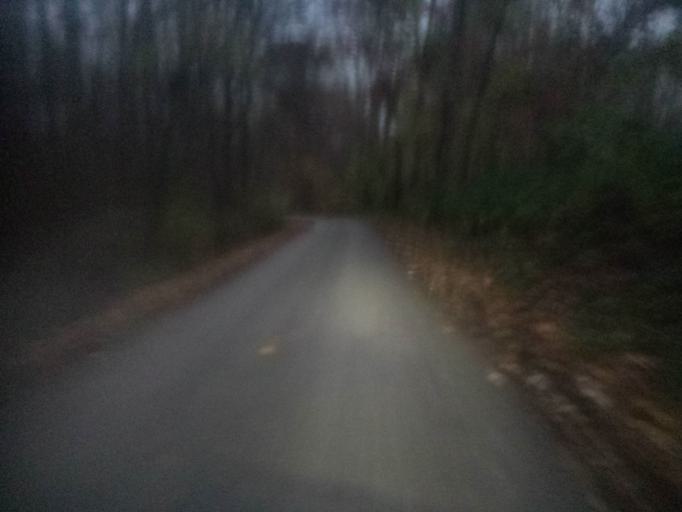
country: DE
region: Bavaria
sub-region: Upper Bavaria
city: Weichering
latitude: 48.7293
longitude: 11.3646
